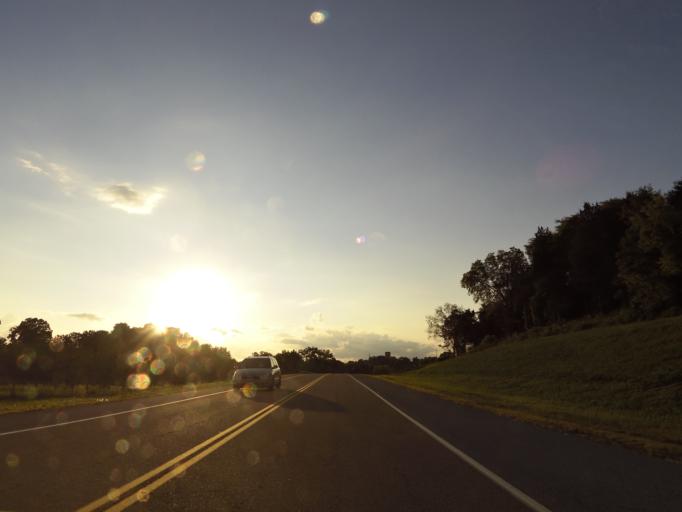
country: US
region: Tennessee
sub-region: Grainger County
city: Blaine
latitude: 36.1602
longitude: -83.7314
